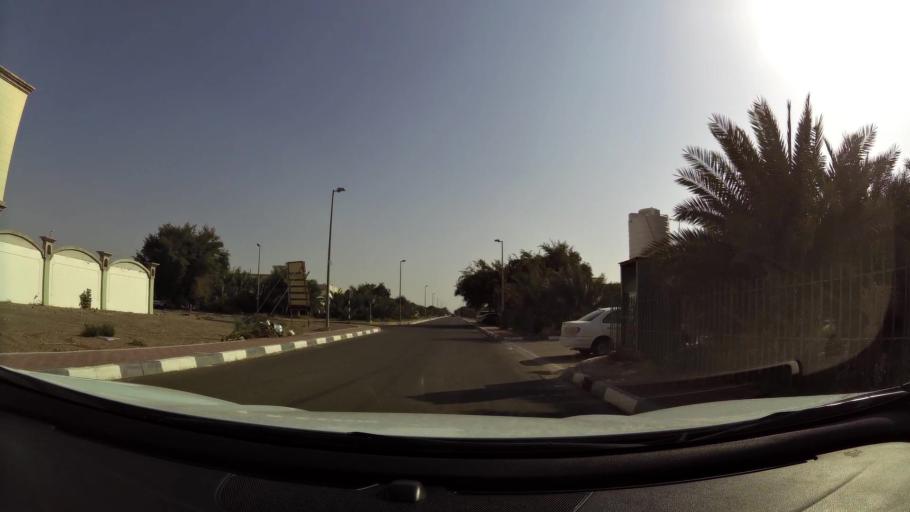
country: AE
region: Abu Dhabi
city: Al Ain
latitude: 24.0815
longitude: 55.8629
